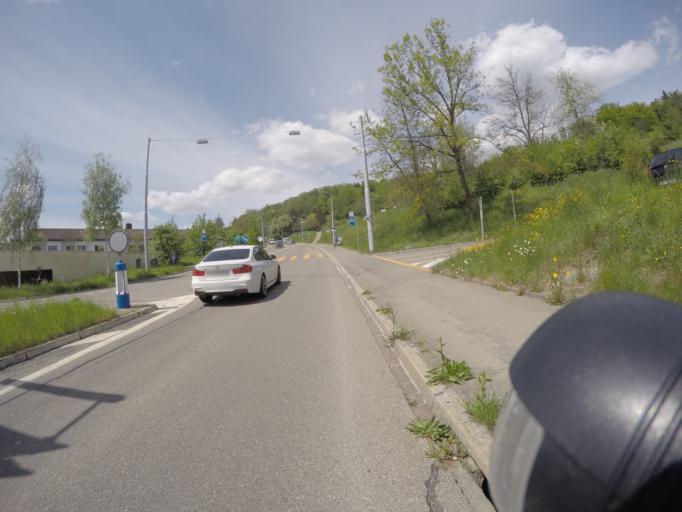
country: CH
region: Zurich
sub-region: Bezirk Zuerich
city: Zuerich (Kreis 10) / Wipkingen
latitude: 47.3994
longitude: 8.5215
